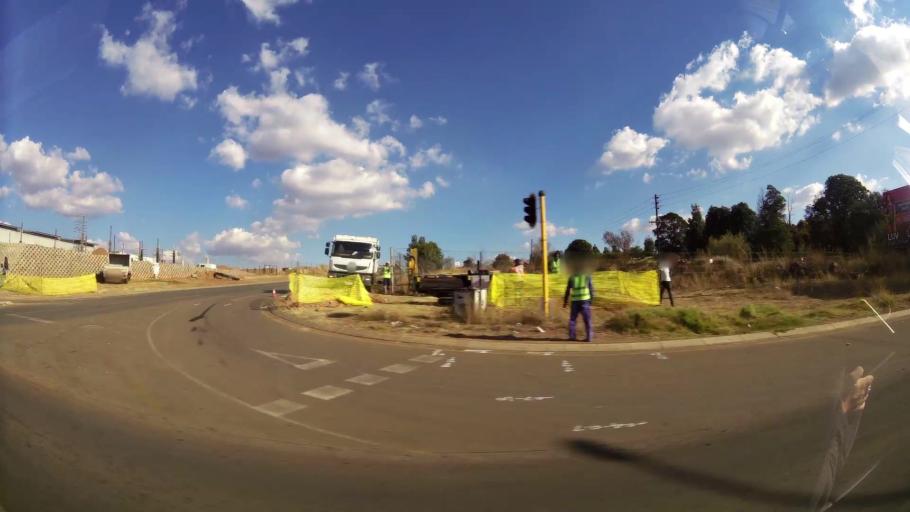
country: ZA
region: Mpumalanga
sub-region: Nkangala District Municipality
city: Witbank
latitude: -25.8796
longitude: 29.2512
